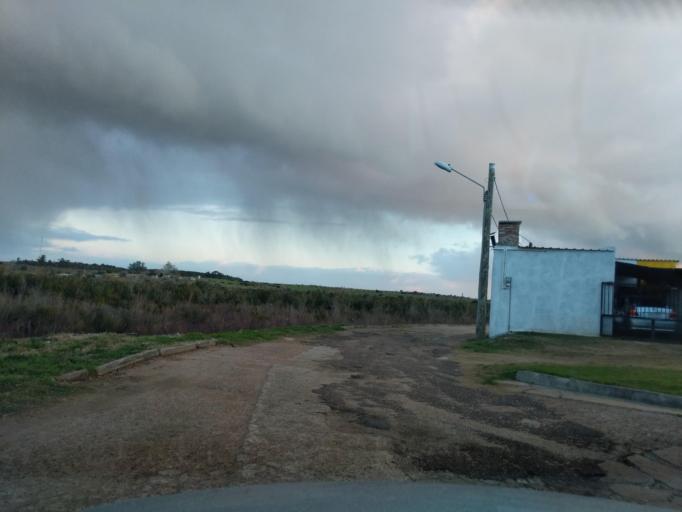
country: UY
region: Florida
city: Florida
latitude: -34.1086
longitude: -56.2066
